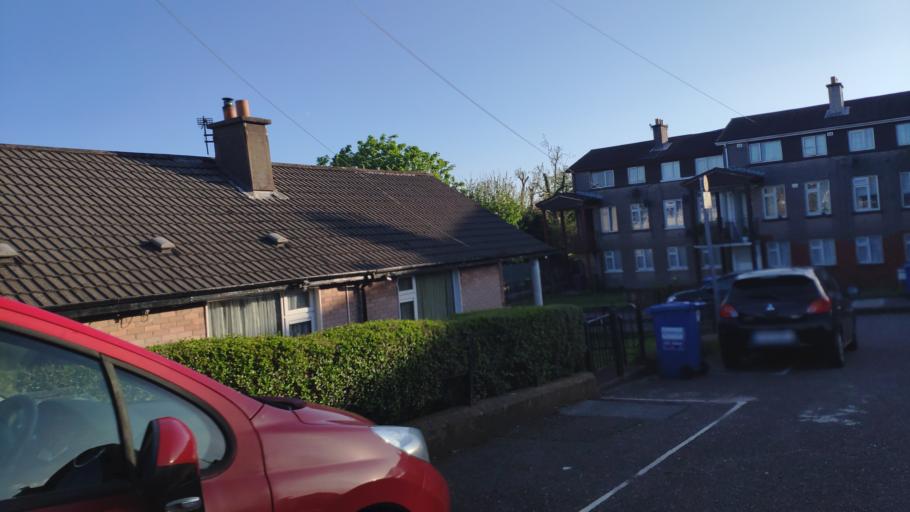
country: IE
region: Munster
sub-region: County Cork
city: Cork
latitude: 51.9060
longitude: -8.4632
